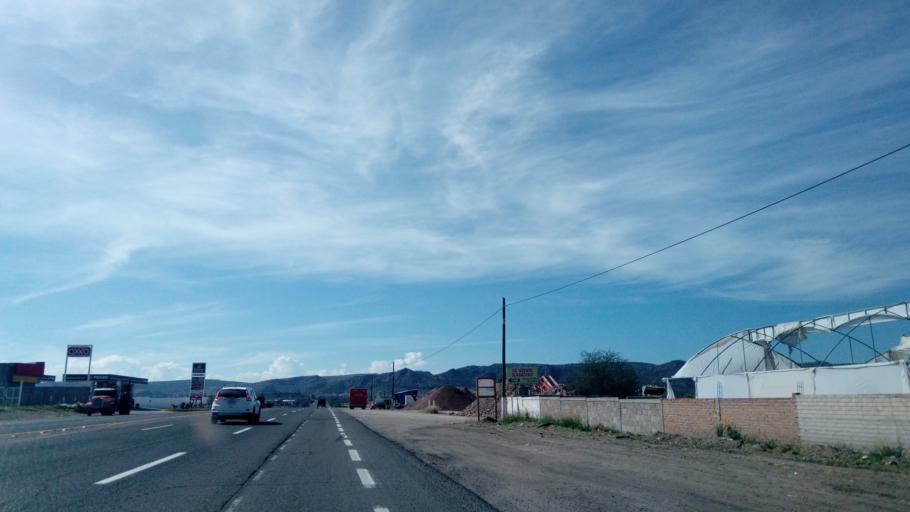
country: MX
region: Durango
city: Victoria de Durango
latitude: 24.1465
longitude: -104.7095
